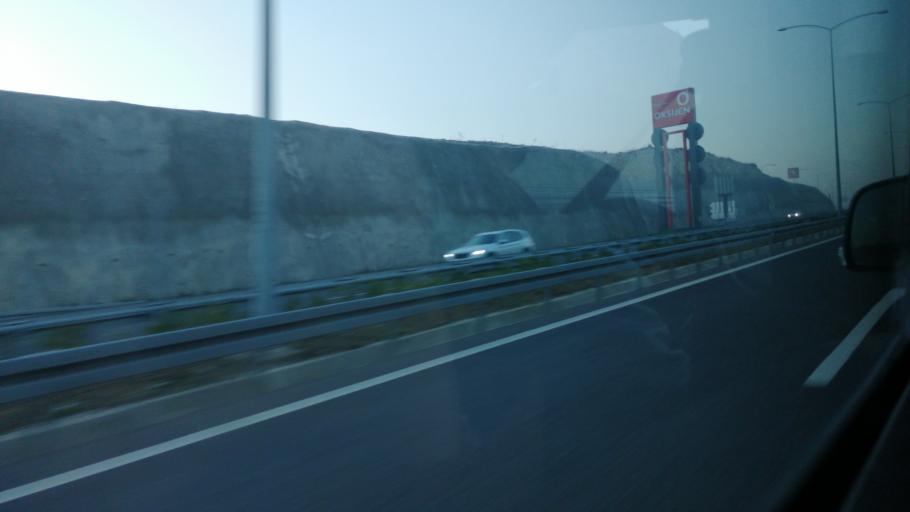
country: TR
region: Kocaeli
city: Tavsanli
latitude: 40.7776
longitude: 29.5183
